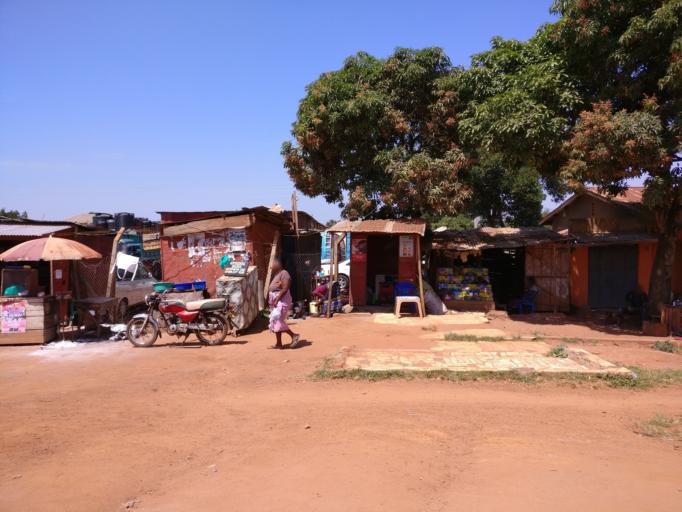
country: UG
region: Central Region
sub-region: Wakiso District
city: Entebbe
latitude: 0.1064
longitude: 32.5207
